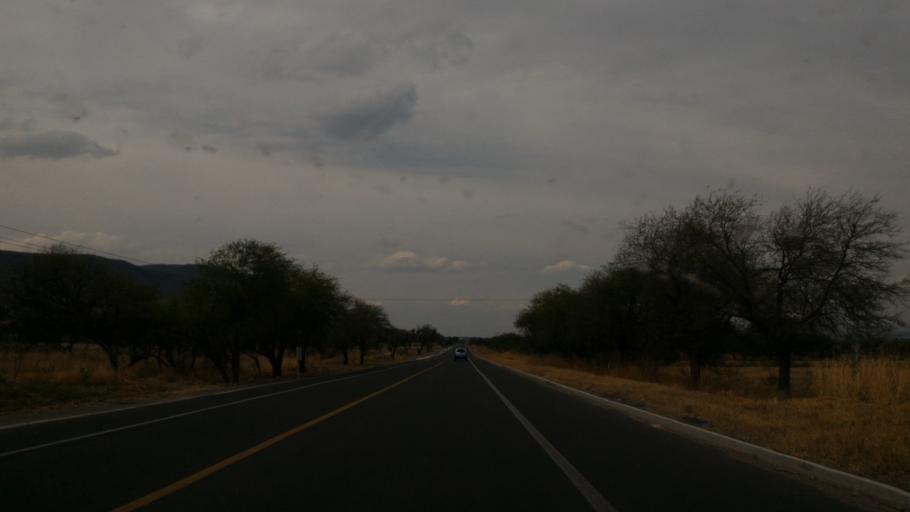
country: MX
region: Guanajuato
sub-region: Purisima del Rincon
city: Monte Grande
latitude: 20.9739
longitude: -101.8963
